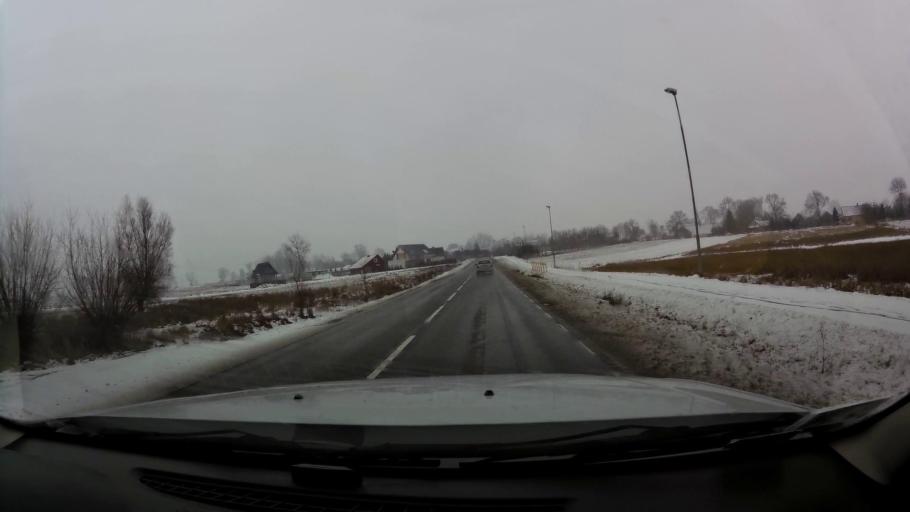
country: PL
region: West Pomeranian Voivodeship
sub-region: Powiat gryficki
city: Trzebiatow
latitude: 54.0945
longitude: 15.2665
